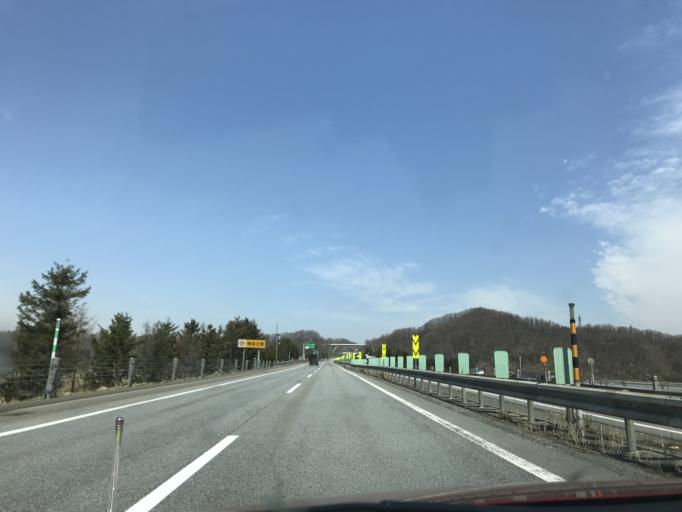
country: JP
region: Hokkaido
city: Iwamizawa
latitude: 43.2388
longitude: 141.8303
